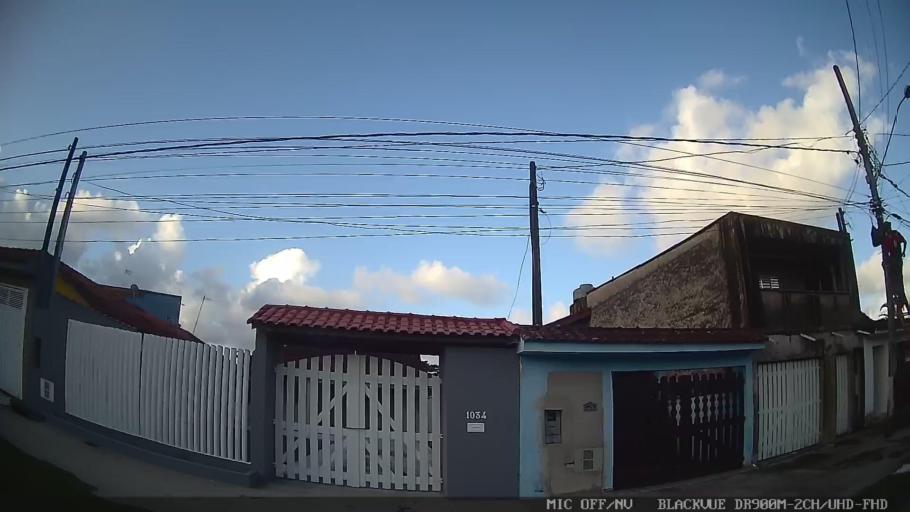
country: BR
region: Sao Paulo
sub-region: Itanhaem
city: Itanhaem
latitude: -24.1393
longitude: -46.7219
